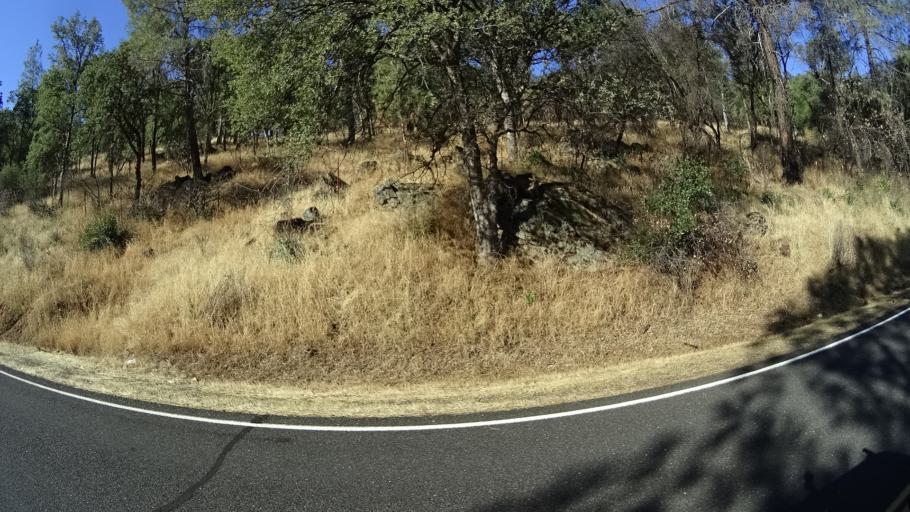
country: US
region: California
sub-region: Calaveras County
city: Angels Camp
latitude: 38.0838
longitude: -120.4838
